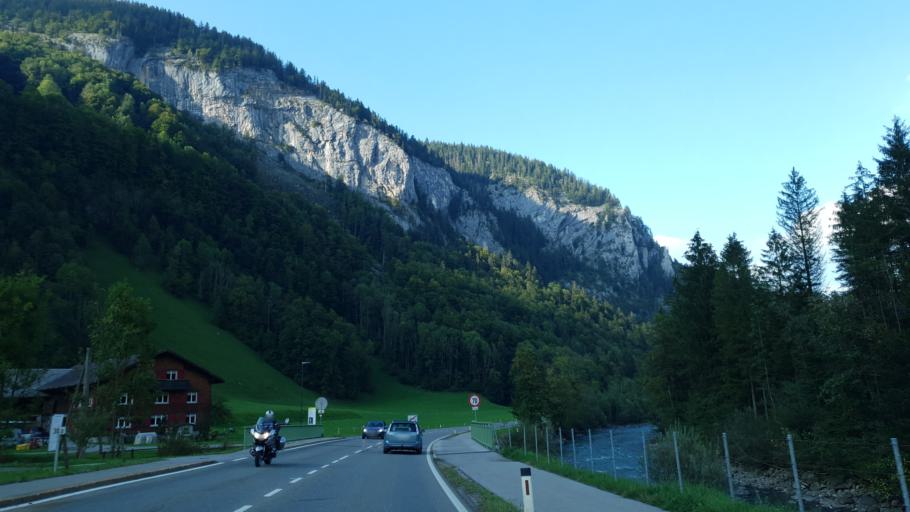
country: AT
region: Vorarlberg
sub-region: Politischer Bezirk Bregenz
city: Reuthe
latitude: 47.3633
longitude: 9.8782
